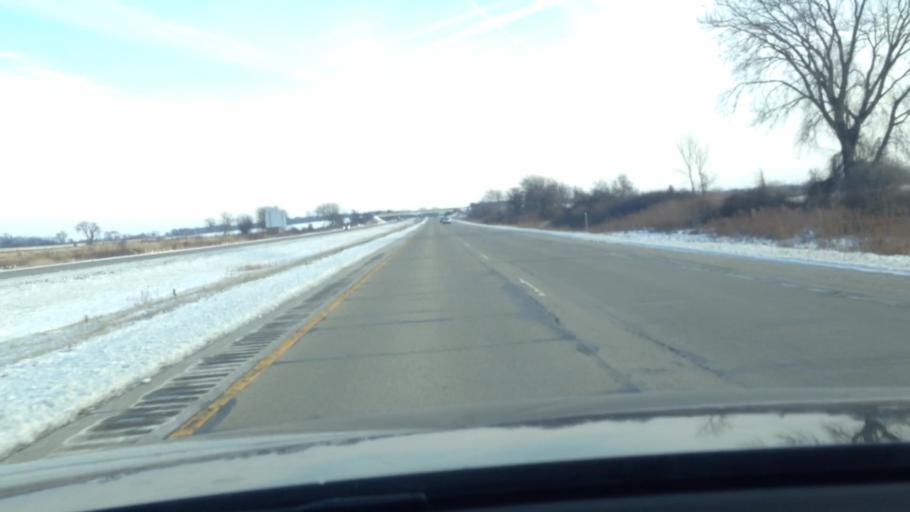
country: US
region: Wisconsin
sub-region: Walworth County
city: Como
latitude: 42.6418
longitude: -88.4944
